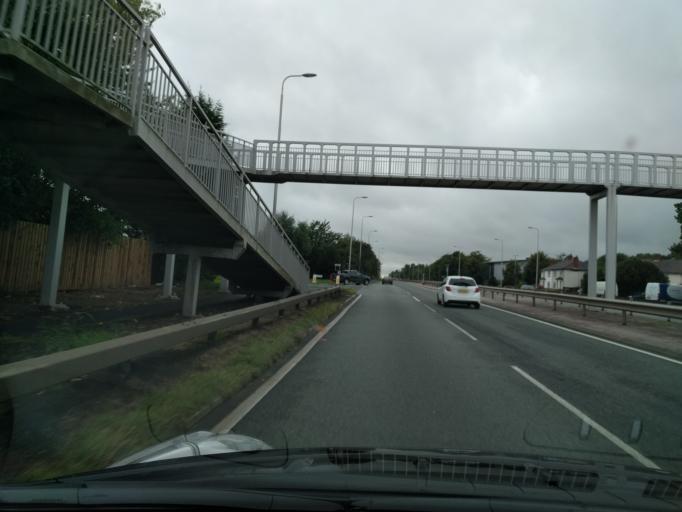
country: GB
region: England
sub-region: Borough of Wigan
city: Ashton in Makerfield
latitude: 53.4724
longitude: -2.6523
